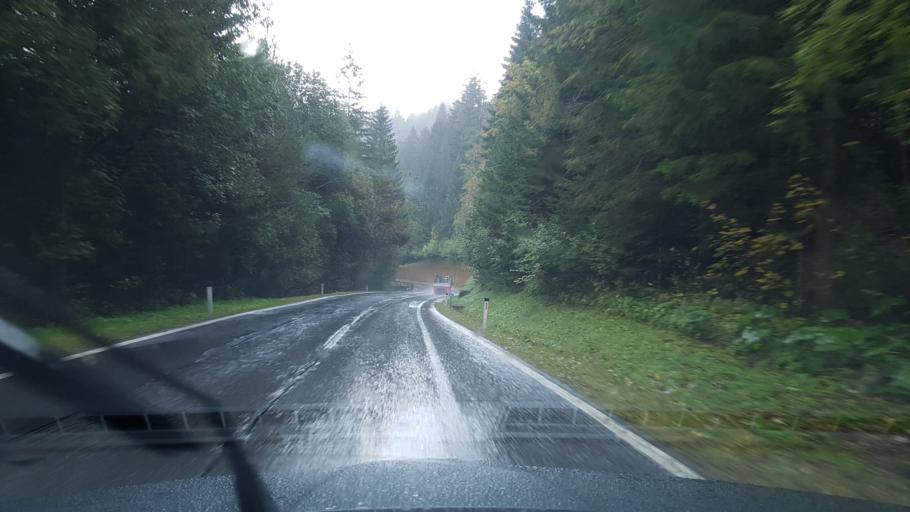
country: AT
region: Styria
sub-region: Politischer Bezirk Voitsberg
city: Salla
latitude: 47.1041
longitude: 14.9606
